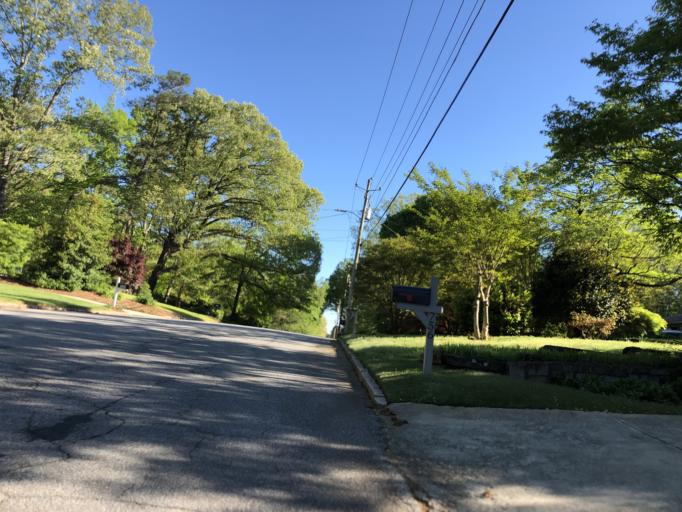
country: US
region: Georgia
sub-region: DeKalb County
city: North Decatur
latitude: 33.7992
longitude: -84.2988
